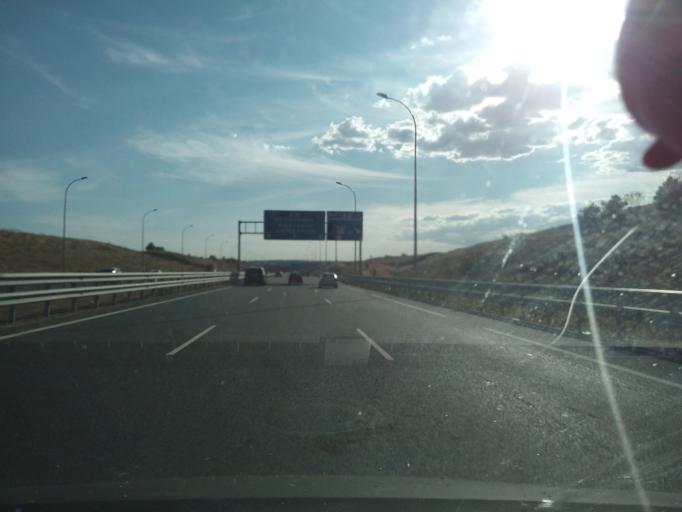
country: ES
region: Madrid
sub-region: Provincia de Madrid
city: Villa de Vallecas
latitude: 40.3384
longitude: -3.6118
